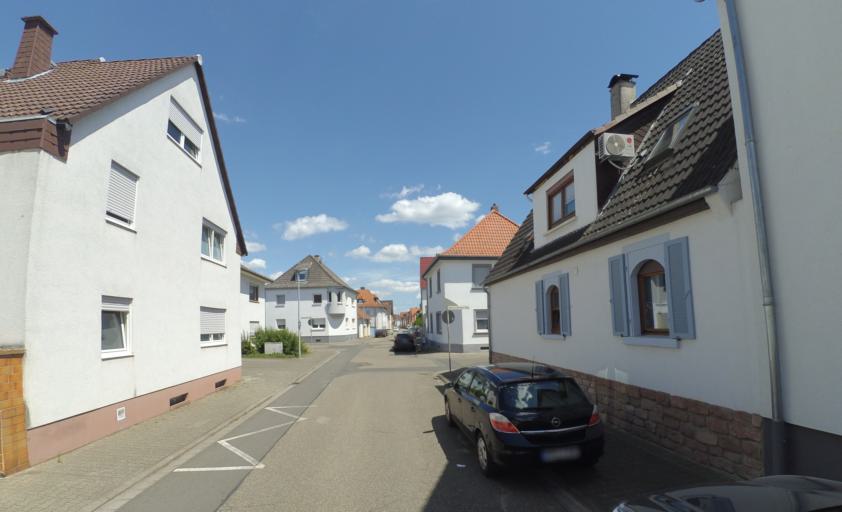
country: DE
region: Hesse
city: Lampertheim
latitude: 49.5991
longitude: 8.4723
